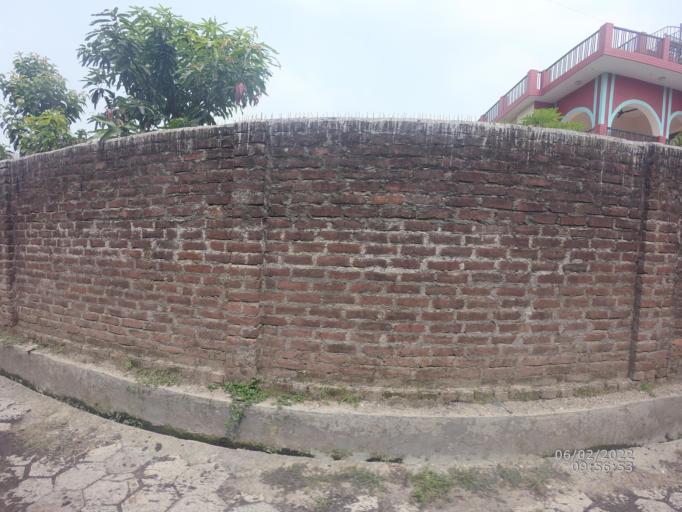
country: NP
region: Western Region
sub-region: Lumbini Zone
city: Bhairahawa
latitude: 27.5026
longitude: 83.4550
